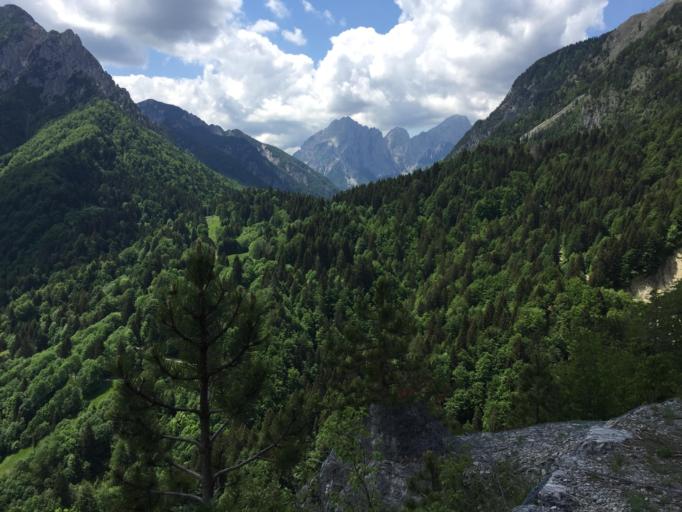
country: IT
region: Friuli Venezia Giulia
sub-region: Provincia di Udine
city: Pontebba
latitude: 46.5093
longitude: 13.2551
